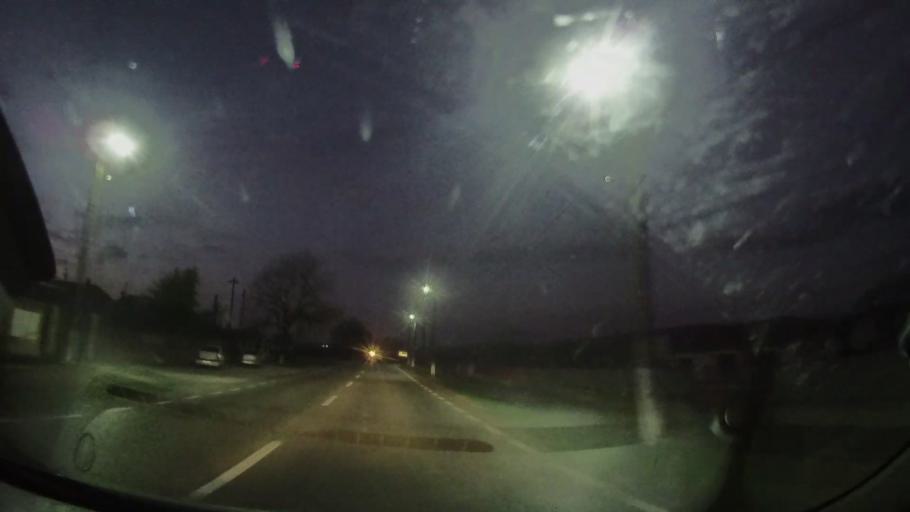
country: RO
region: Tulcea
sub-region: Comuna Mihail Kogalniceanu
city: Mihail Kogalniceanu
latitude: 45.0454
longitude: 28.7359
